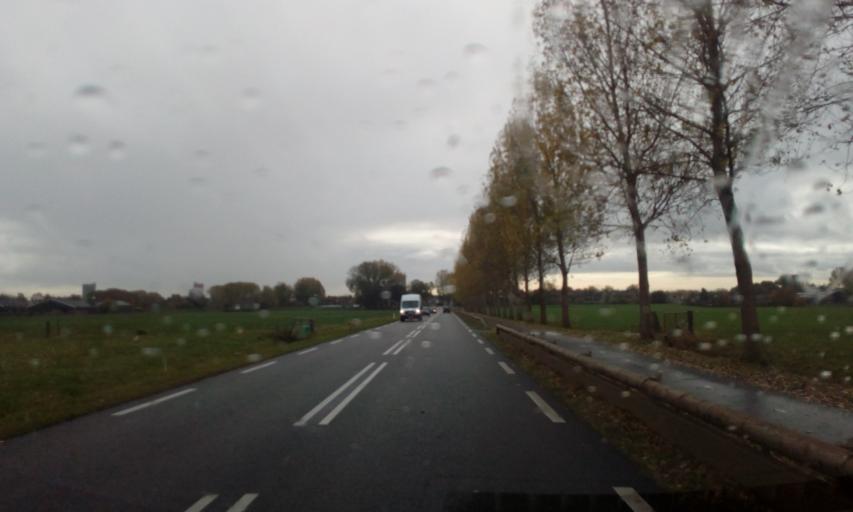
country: NL
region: South Holland
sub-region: Gemeente Zoetermeer
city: Zoetermeer
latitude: 52.0758
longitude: 4.4778
